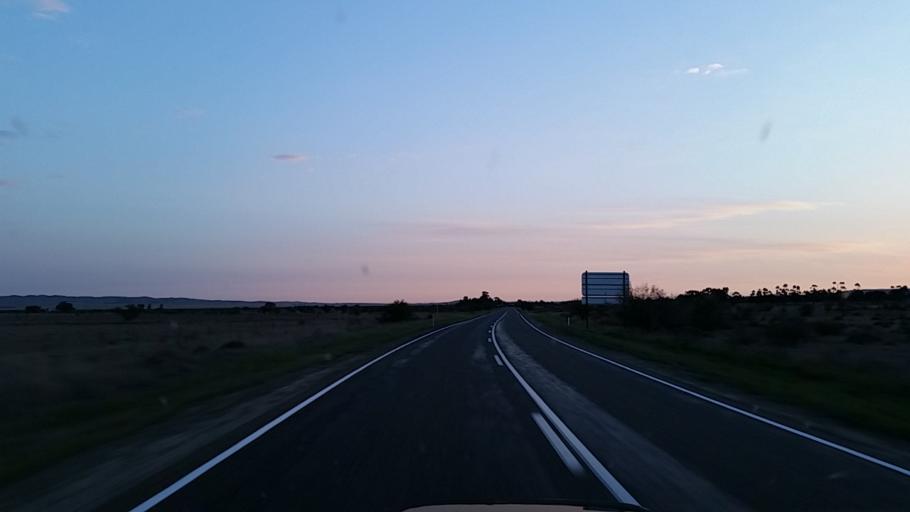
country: AU
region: South Australia
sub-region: Peterborough
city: Peterborough
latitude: -33.1375
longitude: 138.9333
